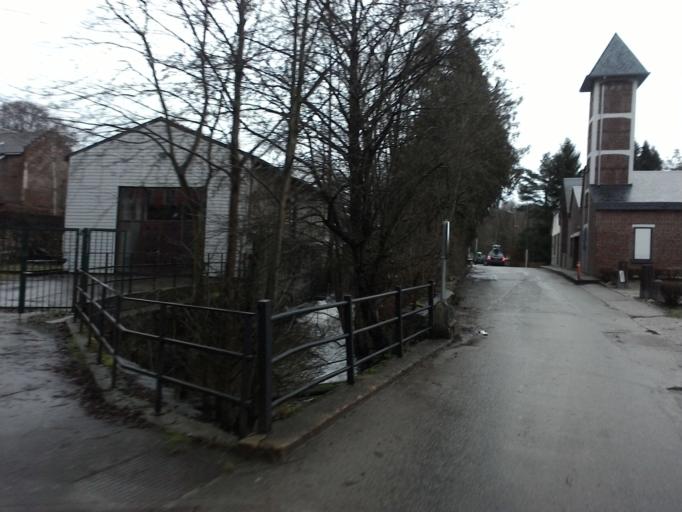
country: BE
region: Wallonia
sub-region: Province de Liege
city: Stavelot
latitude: 50.3934
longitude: 5.9330
